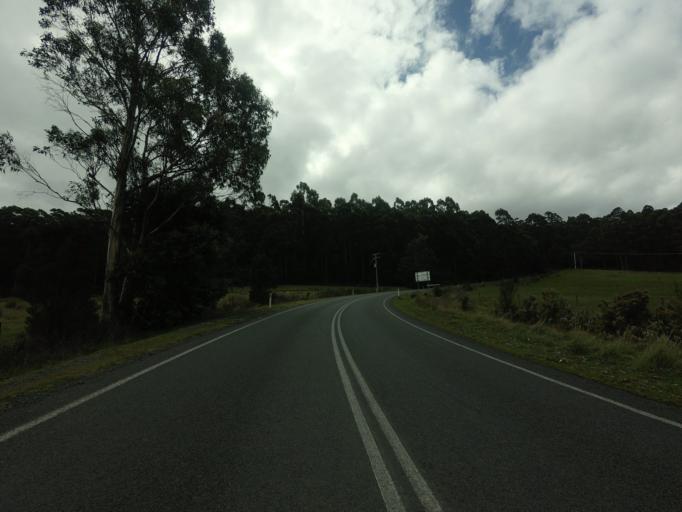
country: AU
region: Tasmania
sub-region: Huon Valley
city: Geeveston
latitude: -43.4114
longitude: 146.9540
